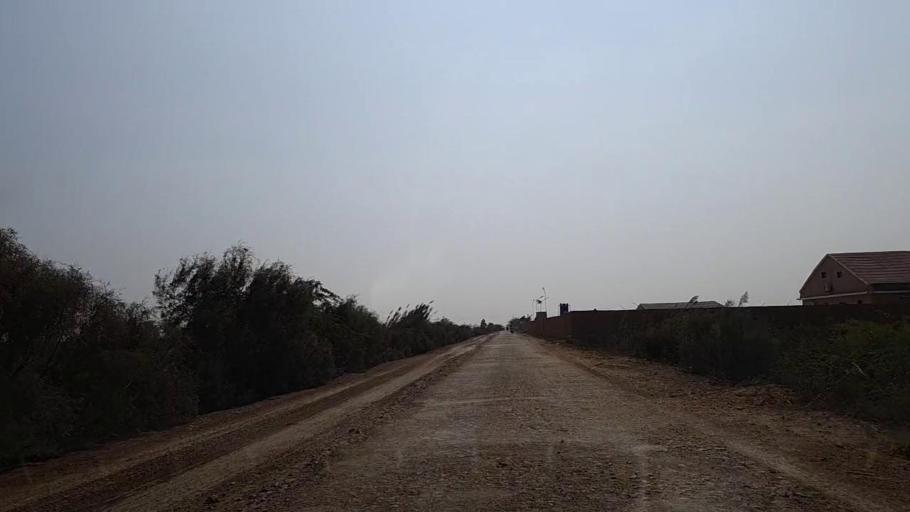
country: PK
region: Sindh
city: Thatta
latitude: 24.7091
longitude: 67.7674
